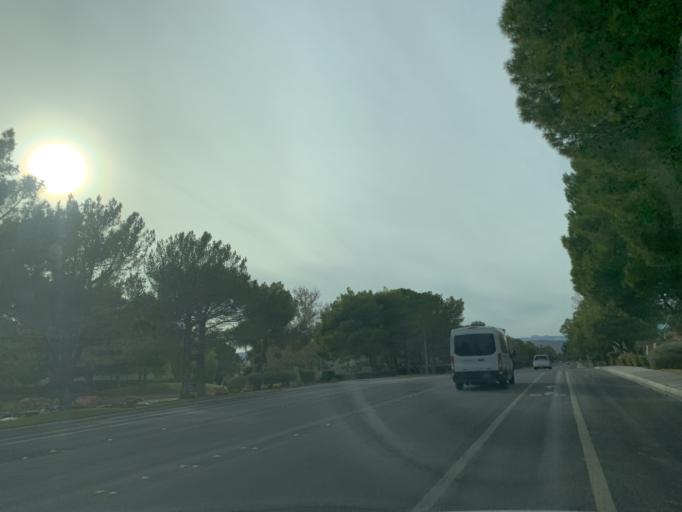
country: US
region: Nevada
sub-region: Clark County
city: Summerlin South
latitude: 36.1408
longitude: -115.3012
